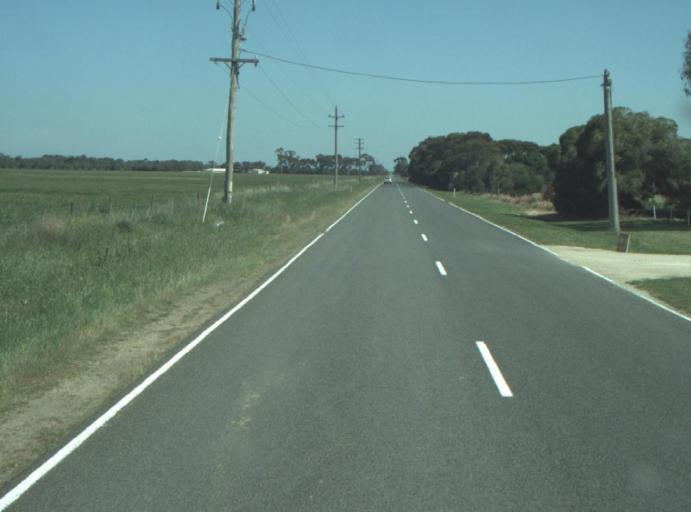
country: AU
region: Victoria
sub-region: Greater Geelong
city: Lara
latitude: -37.9863
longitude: 144.4029
